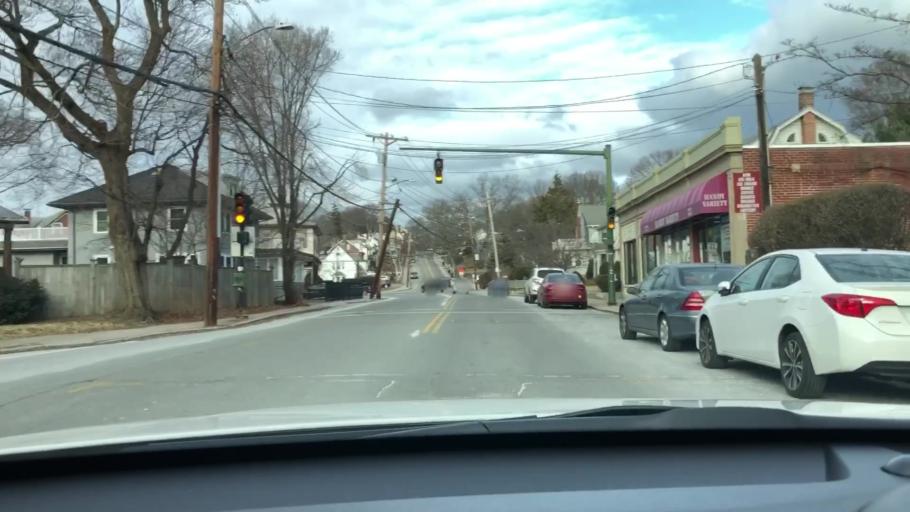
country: US
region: Massachusetts
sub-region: Middlesex County
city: Watertown
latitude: 42.3713
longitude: -71.1789
